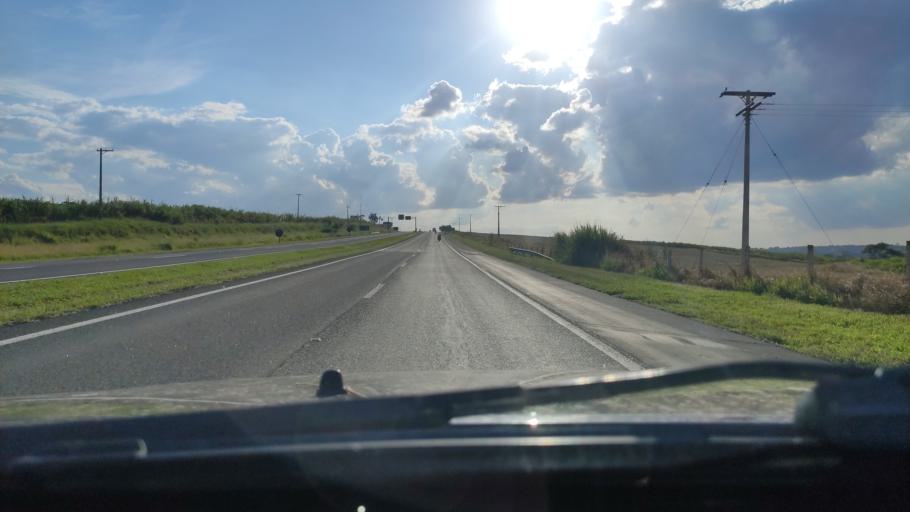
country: BR
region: Sao Paulo
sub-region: Mogi-Mirim
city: Mogi Mirim
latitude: -22.4566
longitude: -46.9080
